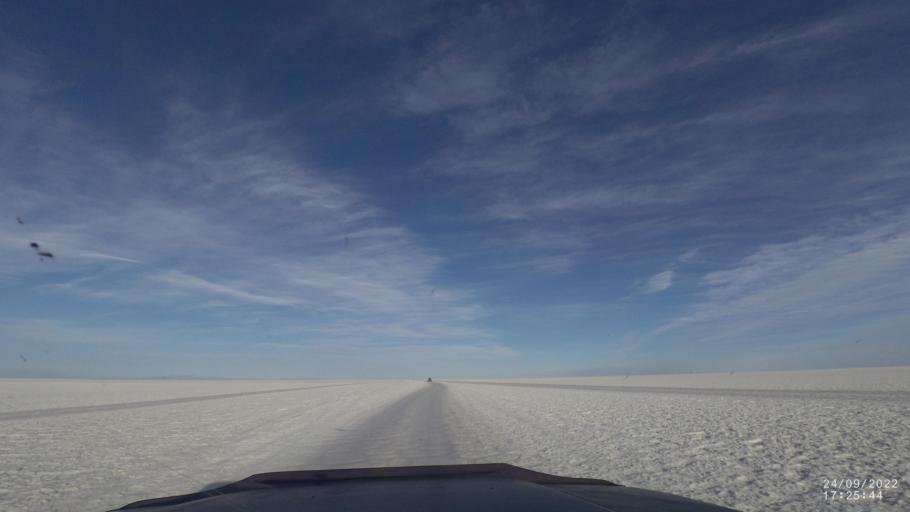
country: BO
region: Potosi
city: Colchani
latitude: -20.2902
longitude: -67.4816
